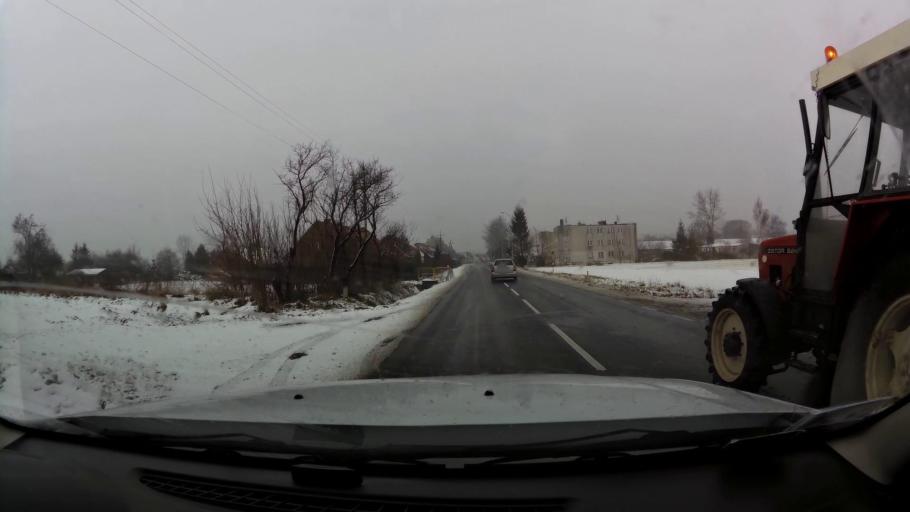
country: PL
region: West Pomeranian Voivodeship
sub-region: Powiat gryficki
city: Trzebiatow
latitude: 54.0790
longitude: 15.2568
